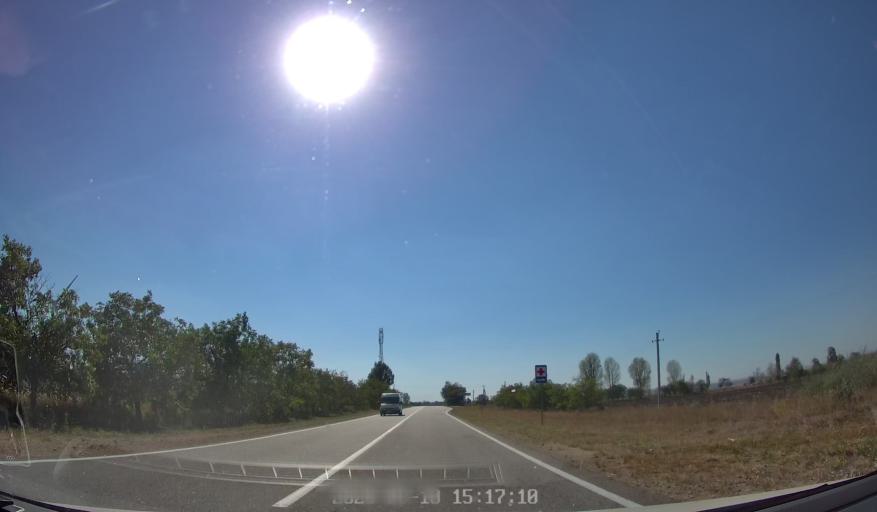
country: MD
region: Rezina
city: Saharna
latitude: 47.5839
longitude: 28.8141
